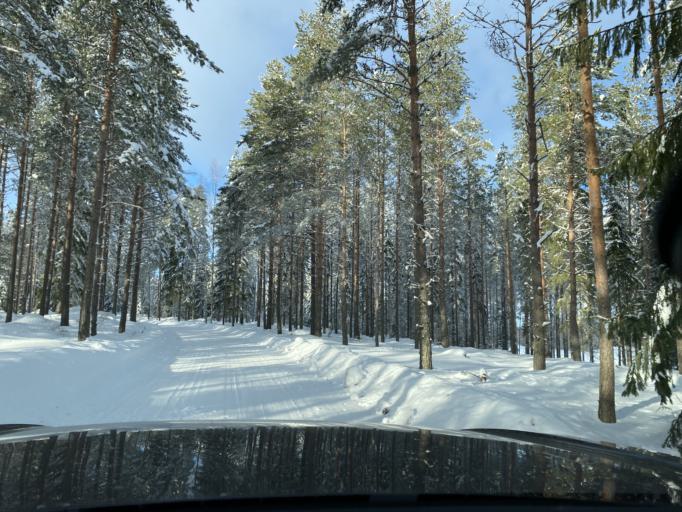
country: FI
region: Pirkanmaa
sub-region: Lounais-Pirkanmaa
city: Punkalaidun
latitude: 61.0721
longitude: 23.2366
